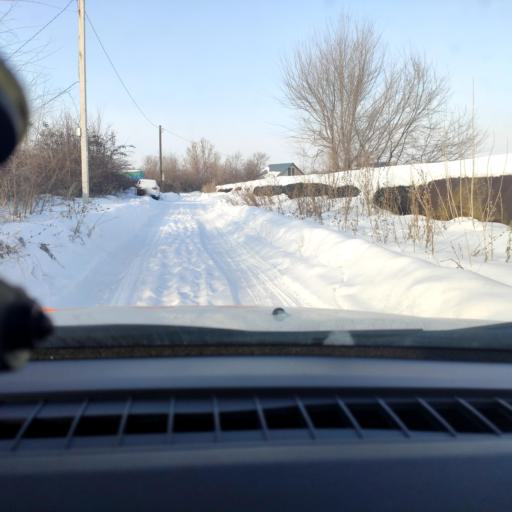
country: RU
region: Samara
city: Samara
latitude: 53.1326
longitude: 50.2588
